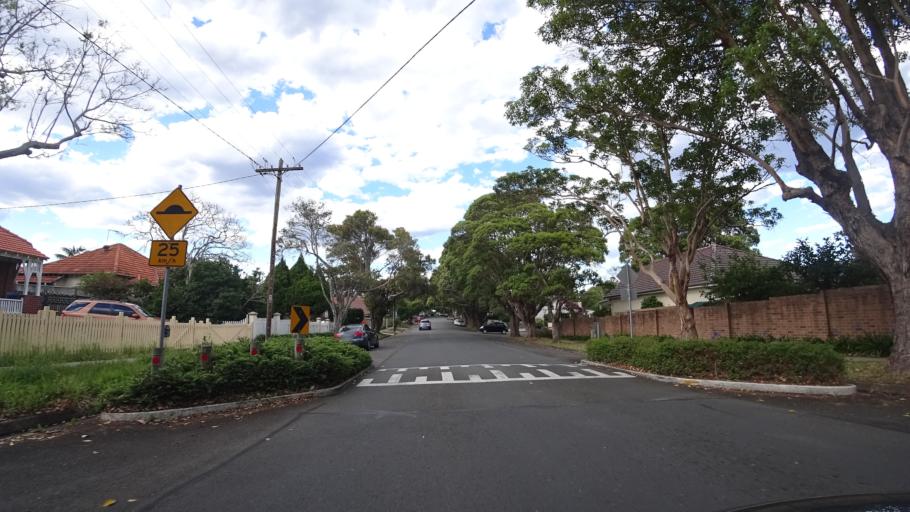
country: AU
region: New South Wales
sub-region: Willoughby
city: Chatswood
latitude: -33.7996
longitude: 151.1920
